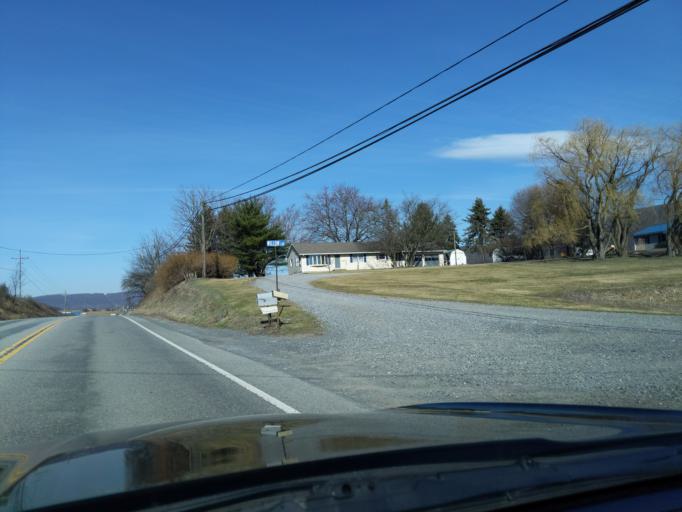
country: US
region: Pennsylvania
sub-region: Blair County
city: Martinsburg
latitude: 40.3197
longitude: -78.3403
